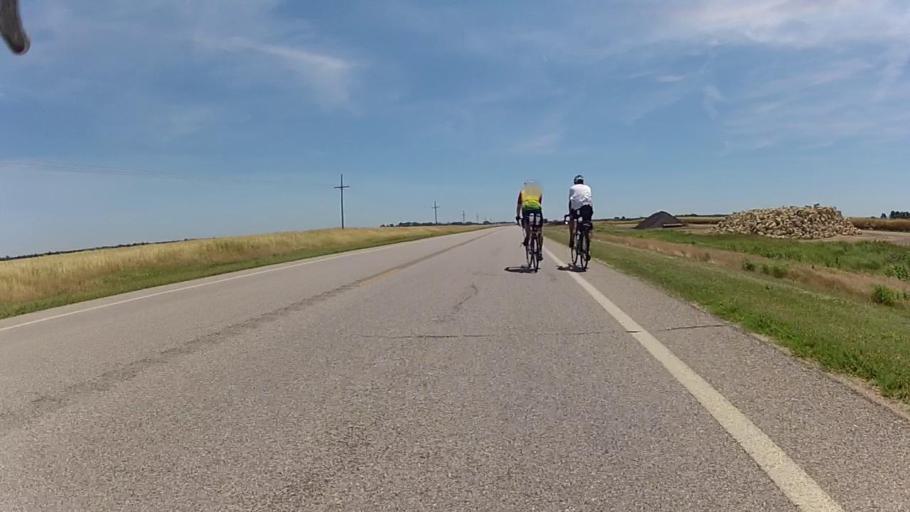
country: US
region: Kansas
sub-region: Barber County
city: Medicine Lodge
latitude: 37.2542
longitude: -98.5070
